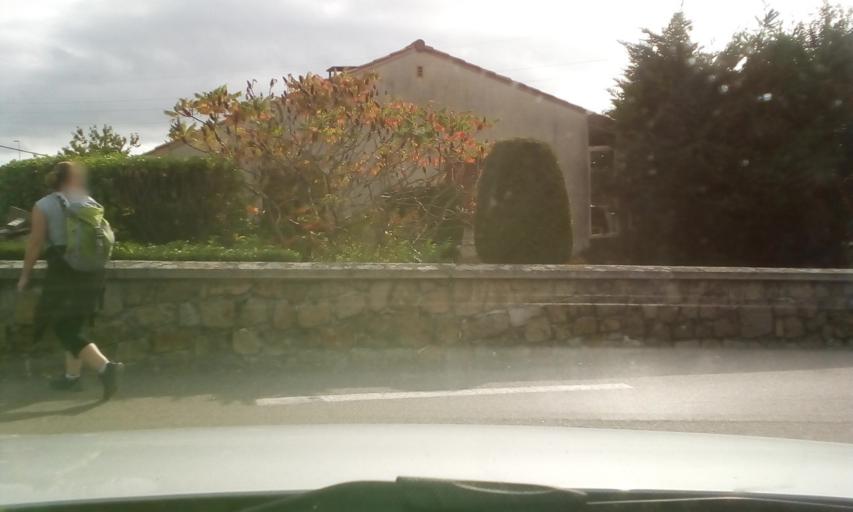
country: FR
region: Rhone-Alpes
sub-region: Departement de l'Ardeche
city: Boulieu-les-Annonay
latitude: 45.2664
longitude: 4.6687
